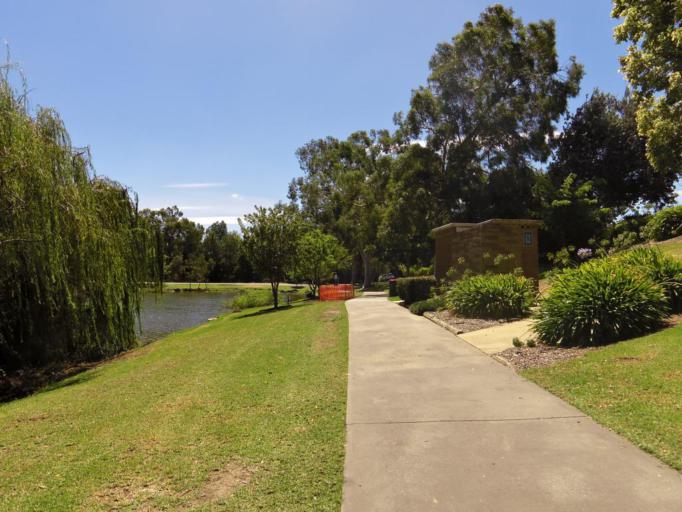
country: AU
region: Victoria
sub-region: Wodonga
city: Wodonga
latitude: -36.1126
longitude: 146.8915
